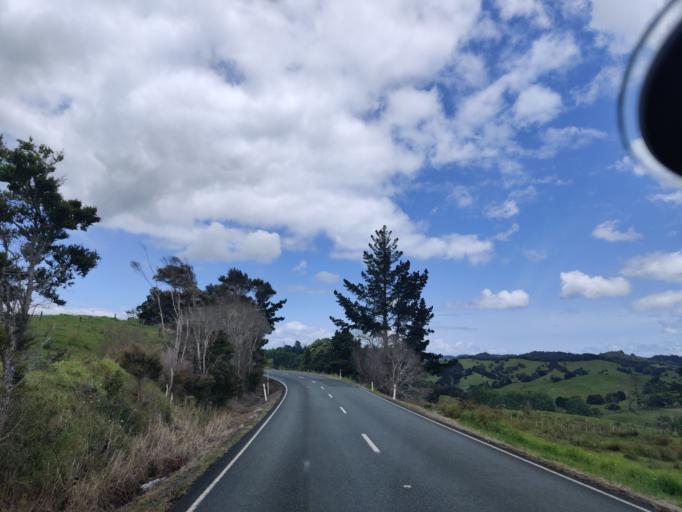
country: NZ
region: Northland
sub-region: Far North District
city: Kaitaia
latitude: -35.2770
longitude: 173.4833
